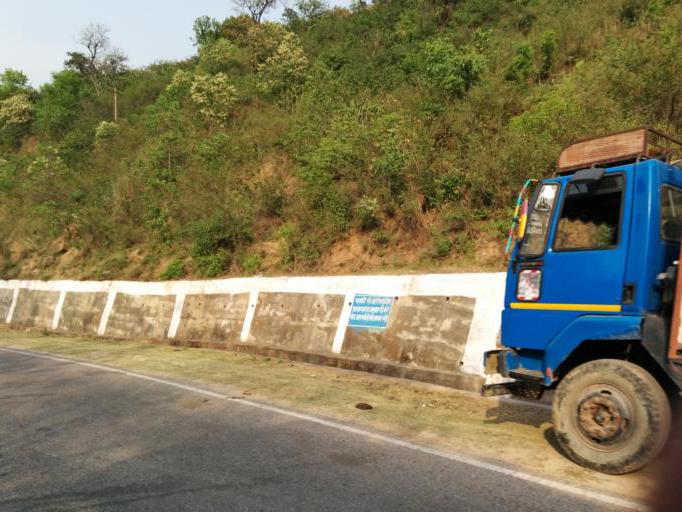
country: IN
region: Himachal Pradesh
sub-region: Kangra
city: Kotla
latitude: 32.2989
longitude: 75.9065
